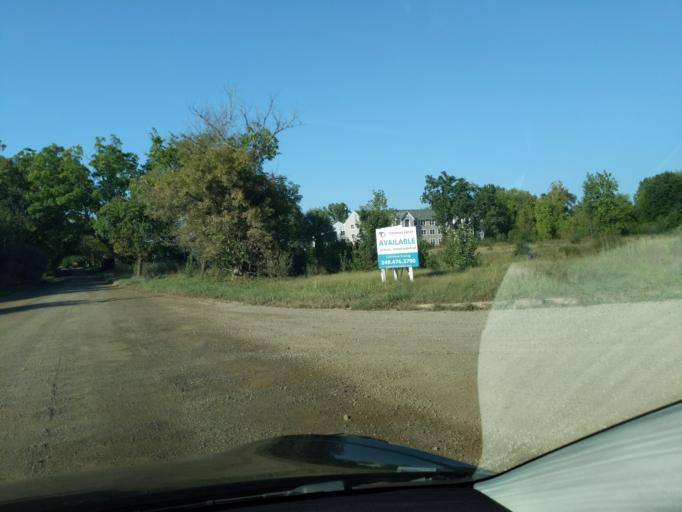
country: US
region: Michigan
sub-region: Oakland County
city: South Lyon
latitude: 42.4582
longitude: -83.6665
